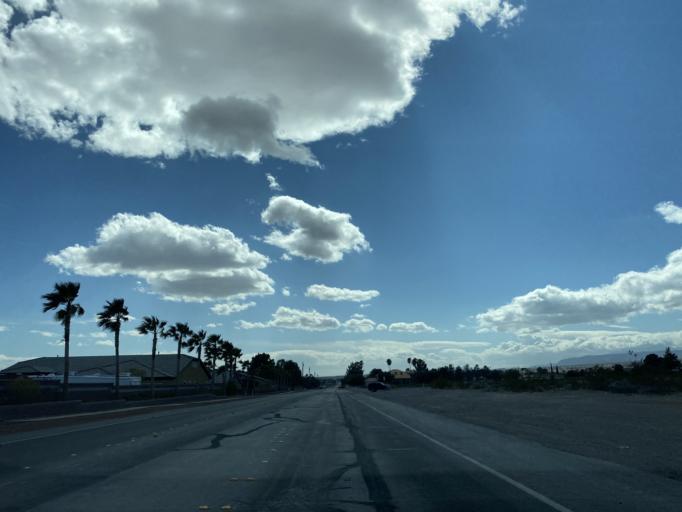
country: US
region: Nevada
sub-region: Clark County
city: Summerlin South
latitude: 36.2549
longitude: -115.2884
